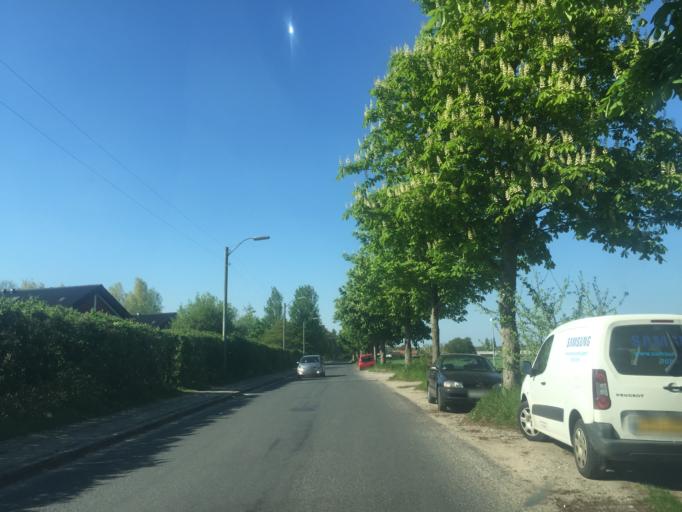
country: DK
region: South Denmark
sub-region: Odense Kommune
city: Hojby
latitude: 55.3577
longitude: 10.4072
